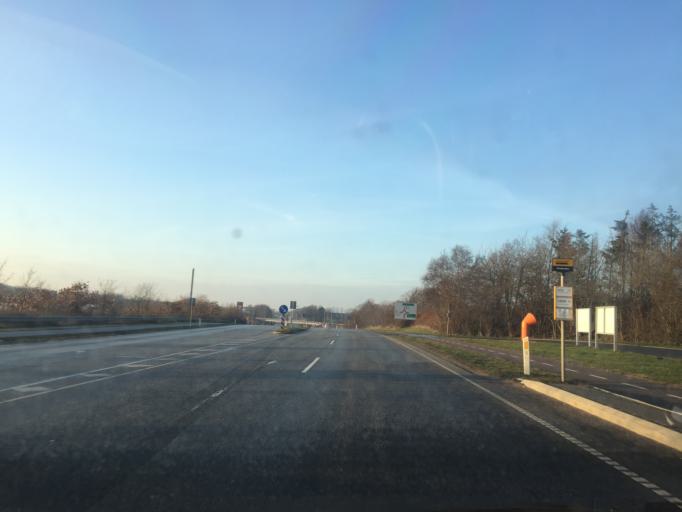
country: DK
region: Zealand
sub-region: Slagelse Kommune
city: Slagelse
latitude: 55.3867
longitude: 11.3674
